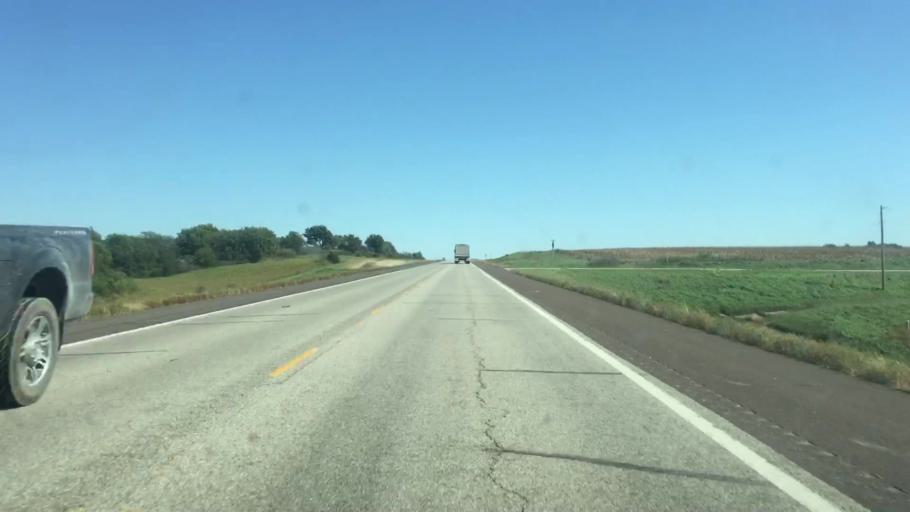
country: US
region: Kansas
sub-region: Nemaha County
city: Seneca
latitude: 39.8411
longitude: -96.2118
